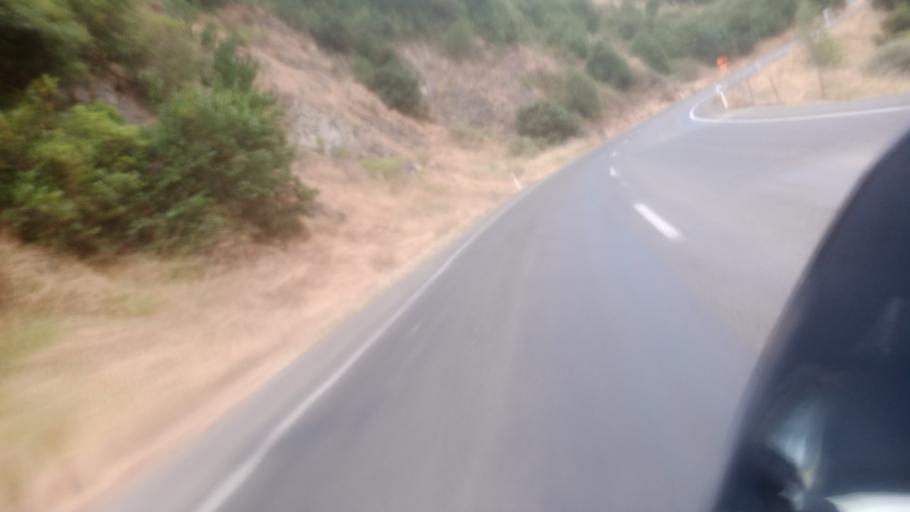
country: NZ
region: Bay of Plenty
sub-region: Opotiki District
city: Opotiki
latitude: -38.3791
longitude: 177.4786
